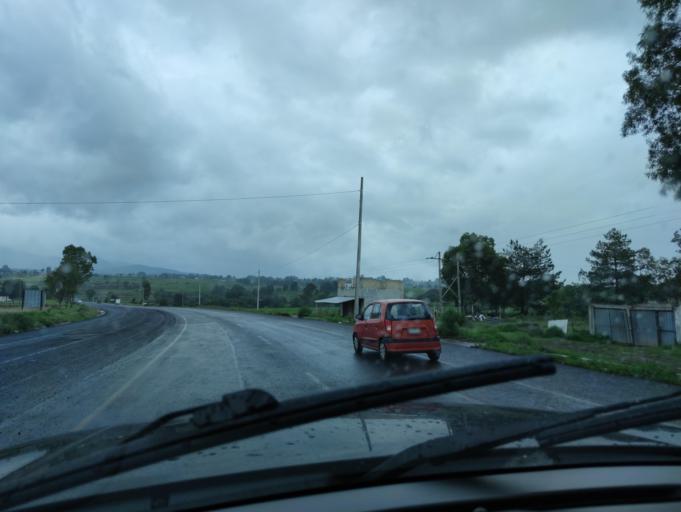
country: MX
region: Mexico
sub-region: Jilotepec
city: Doxhicho
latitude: 19.9106
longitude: -99.6091
